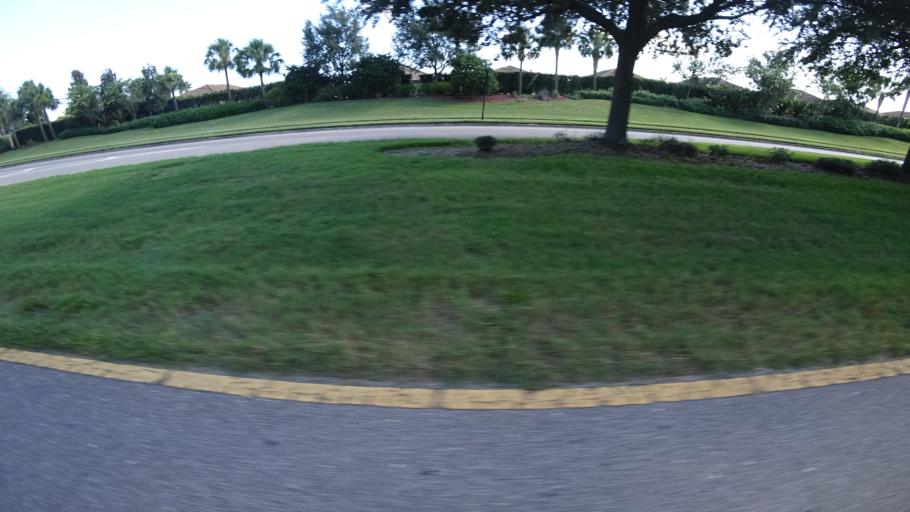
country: US
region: Florida
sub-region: Manatee County
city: Ellenton
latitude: 27.5058
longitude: -82.4768
